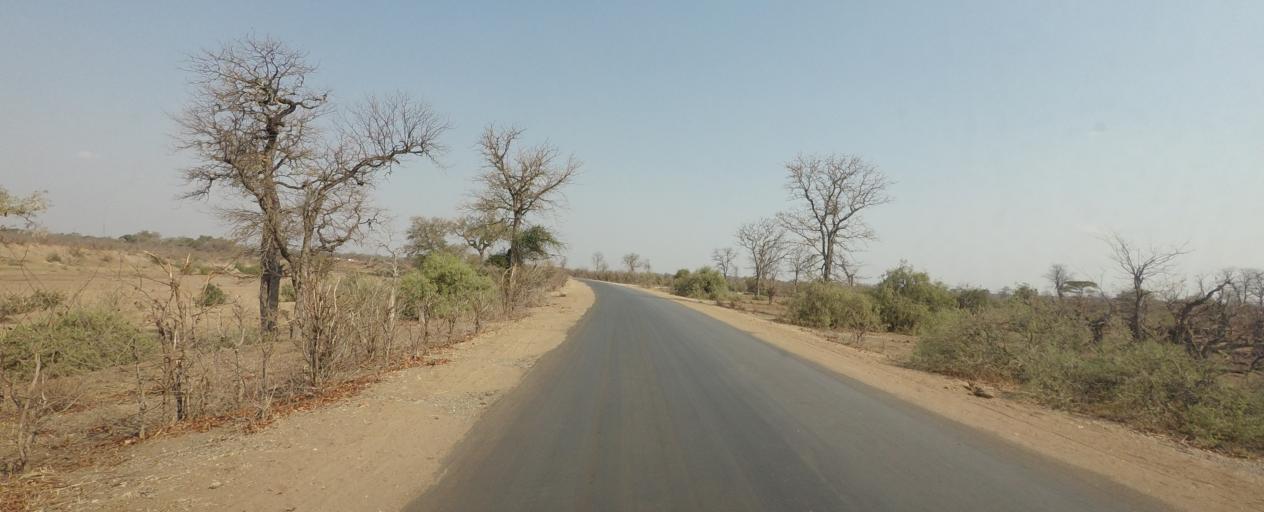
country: ZA
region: Limpopo
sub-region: Mopani District Municipality
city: Giyani
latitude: -23.1032
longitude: 31.4278
